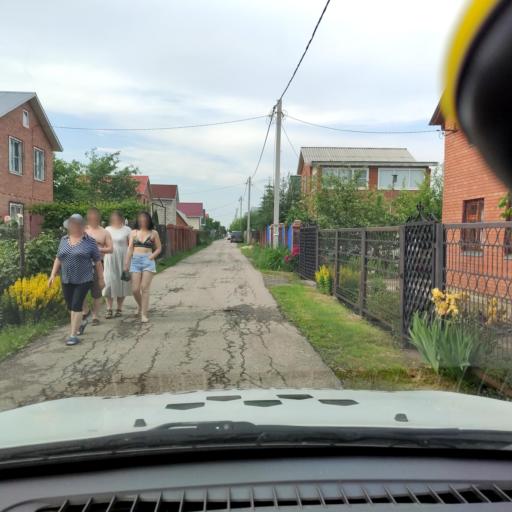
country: RU
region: Samara
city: Podstepki
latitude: 53.5771
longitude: 49.0792
